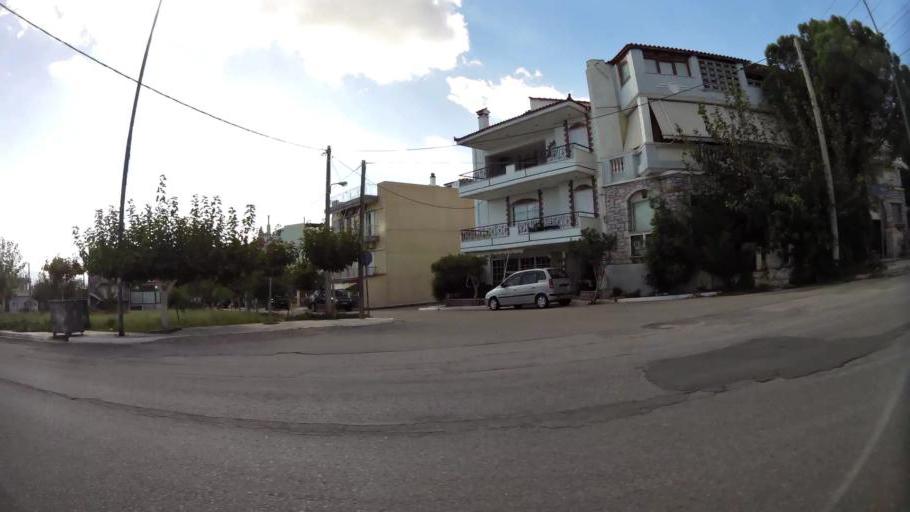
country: GR
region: Attica
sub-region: Nomarchia Anatolikis Attikis
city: Acharnes
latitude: 38.1035
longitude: 23.7396
